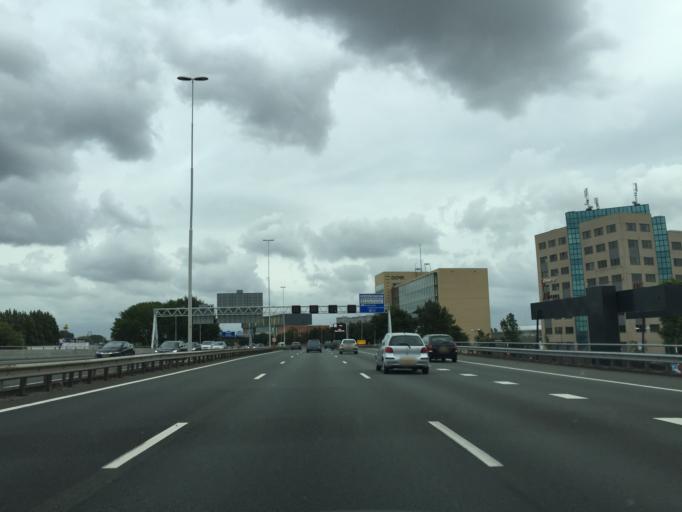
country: NL
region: South Holland
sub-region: Gemeente Schiedam
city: Schiedam
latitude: 51.9245
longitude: 4.4073
